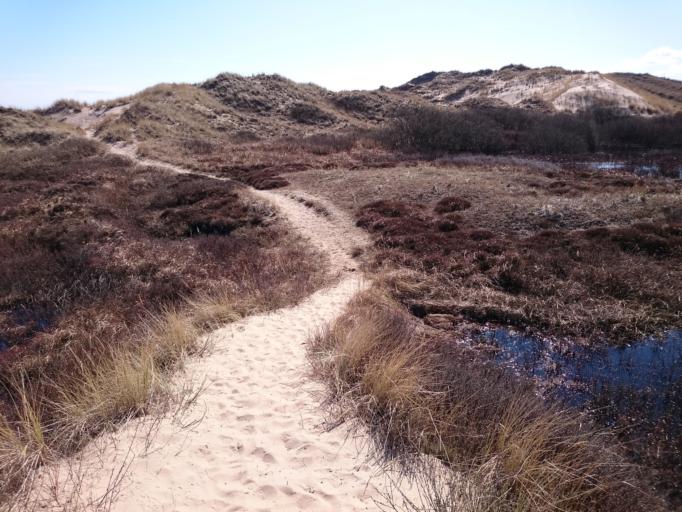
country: DK
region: North Denmark
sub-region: Frederikshavn Kommune
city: Skagen
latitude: 57.6935
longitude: 10.5266
